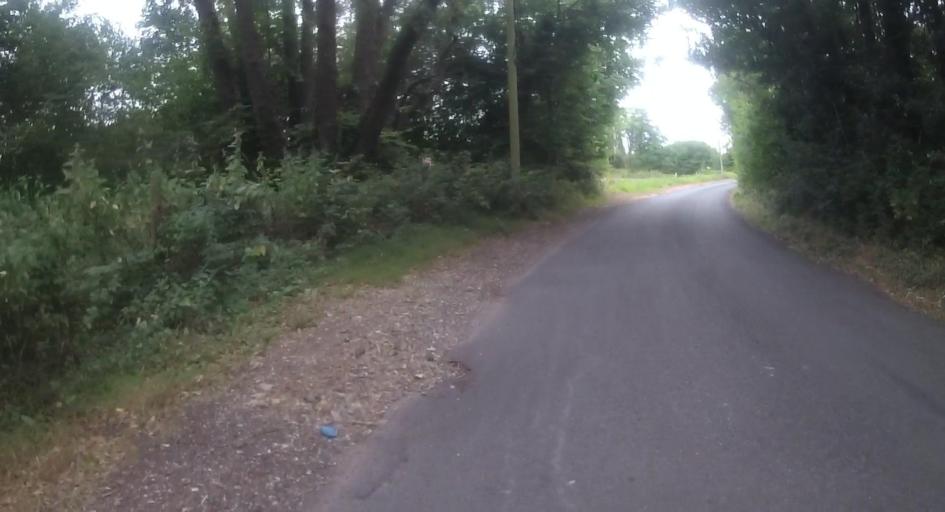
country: GB
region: England
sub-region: Dorset
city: Bovington Camp
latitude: 50.7350
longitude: -2.2303
